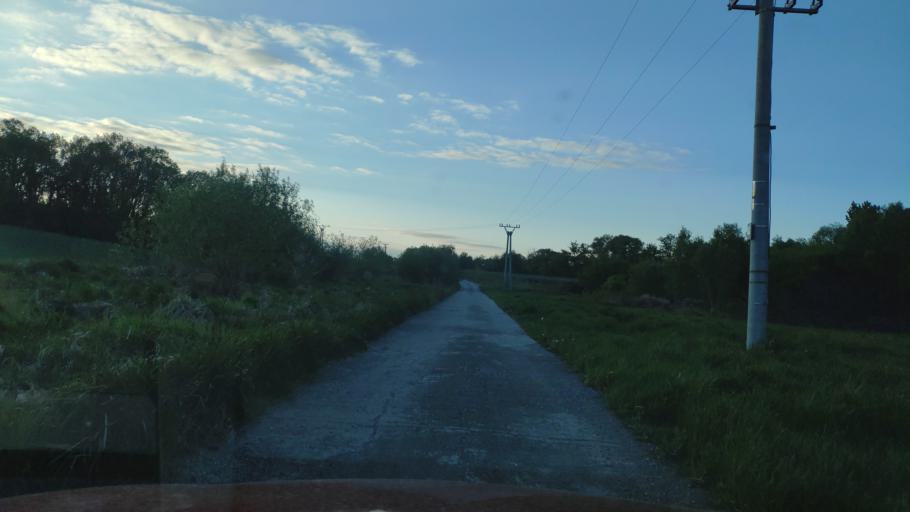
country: SK
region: Kosicky
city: Kosice
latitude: 48.7339
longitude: 21.4207
